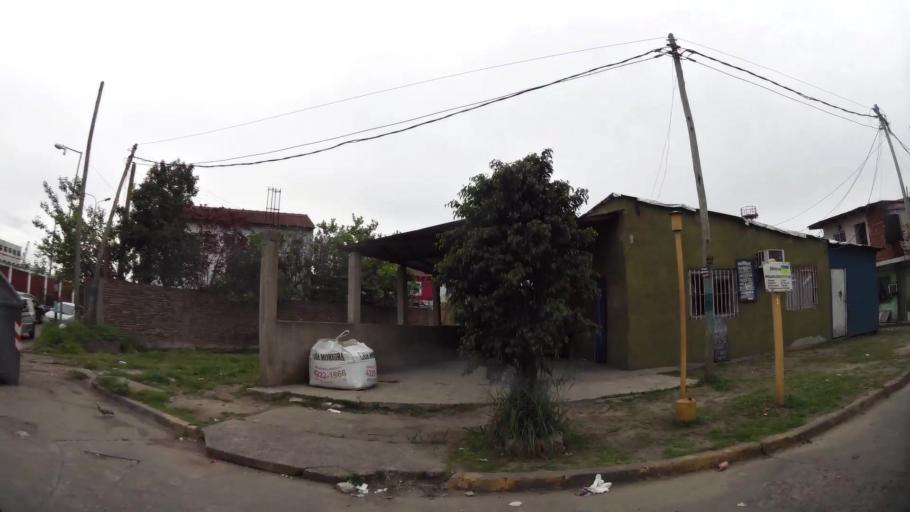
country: AR
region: Buenos Aires
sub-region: Partido de Avellaneda
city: Avellaneda
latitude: -34.6429
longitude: -58.3494
